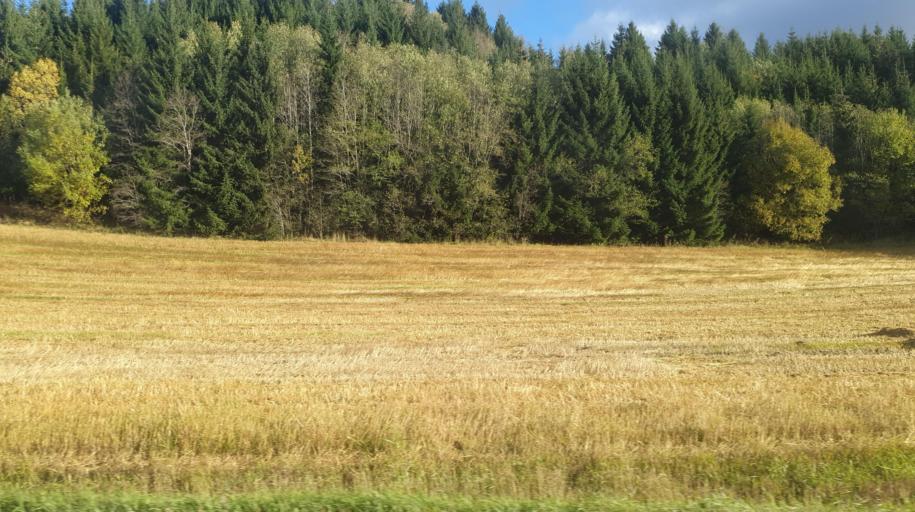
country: NO
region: Sor-Trondelag
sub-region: Klaebu
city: Klaebu
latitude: 63.3094
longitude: 10.4555
